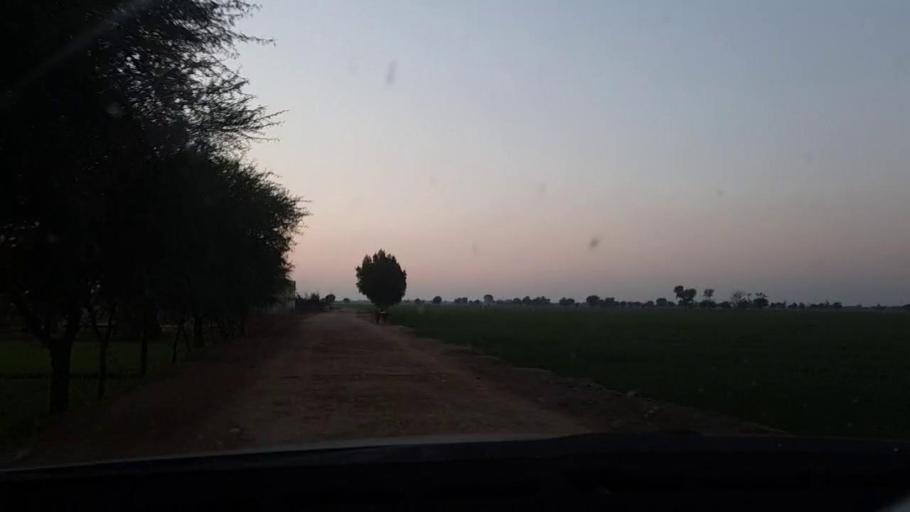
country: PK
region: Sindh
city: Tando Mittha Khan
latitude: 25.9302
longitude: 69.3290
